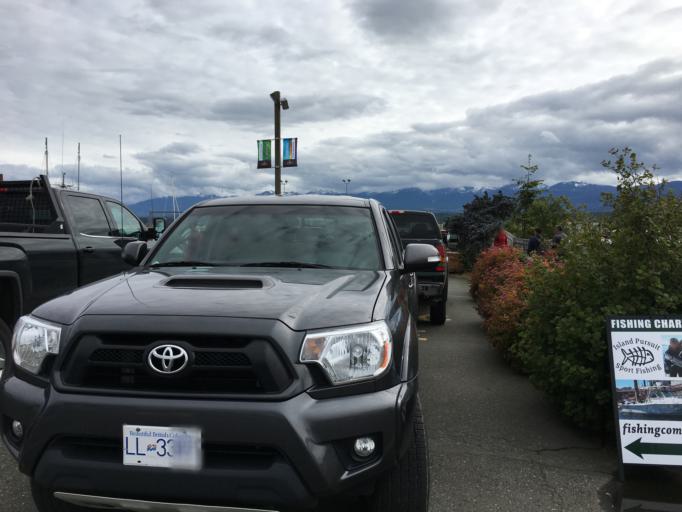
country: CA
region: British Columbia
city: Courtenay
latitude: 49.6695
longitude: -124.9271
